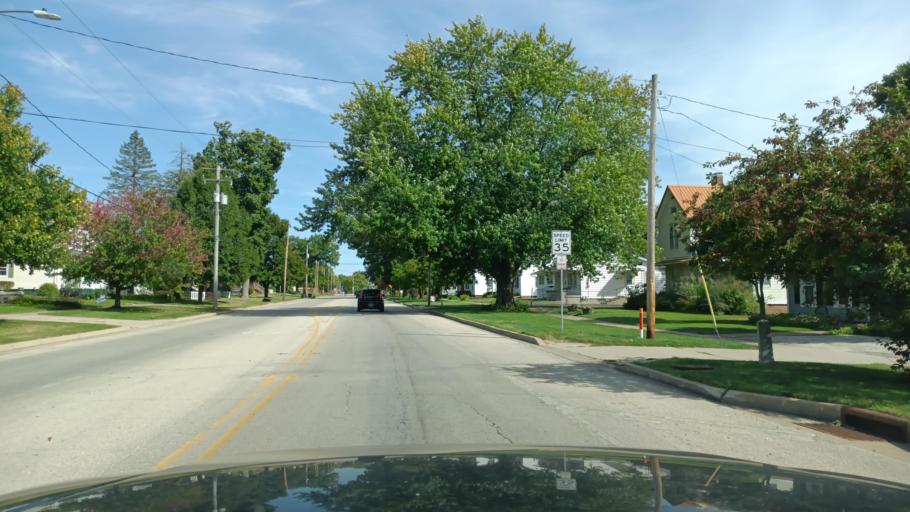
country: US
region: Illinois
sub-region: Knox County
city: Knoxville
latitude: 40.9081
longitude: -90.2889
